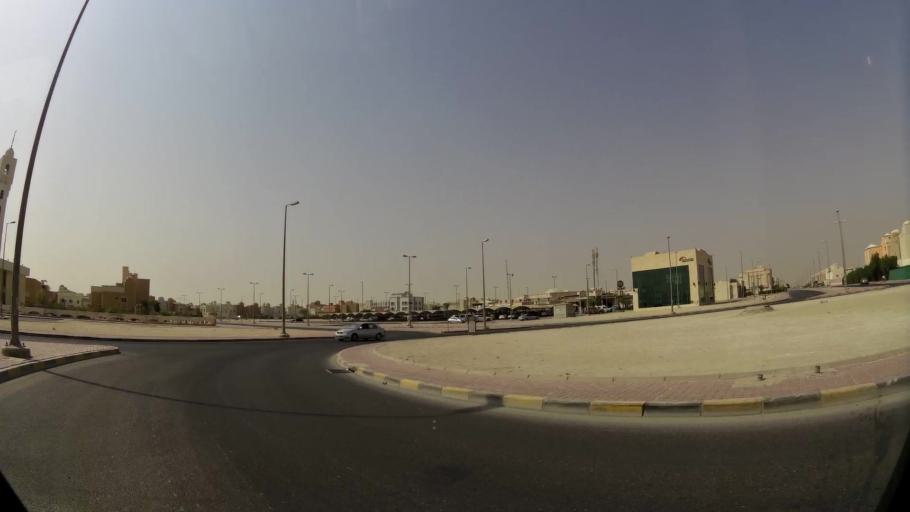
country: KW
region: Muhafazat al Jahra'
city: Al Jahra'
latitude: 29.3203
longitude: 47.7251
